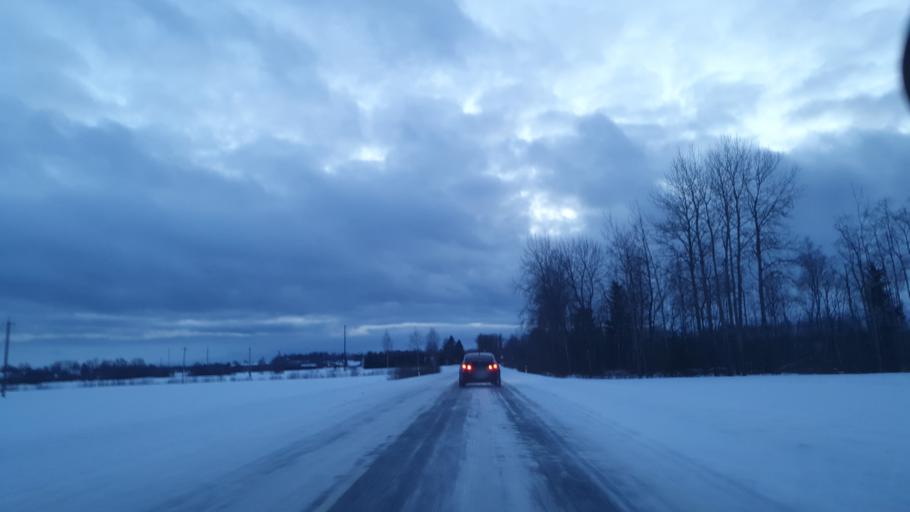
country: EE
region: Jogevamaa
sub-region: Jogeva linn
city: Jogeva
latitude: 58.5831
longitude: 26.3134
